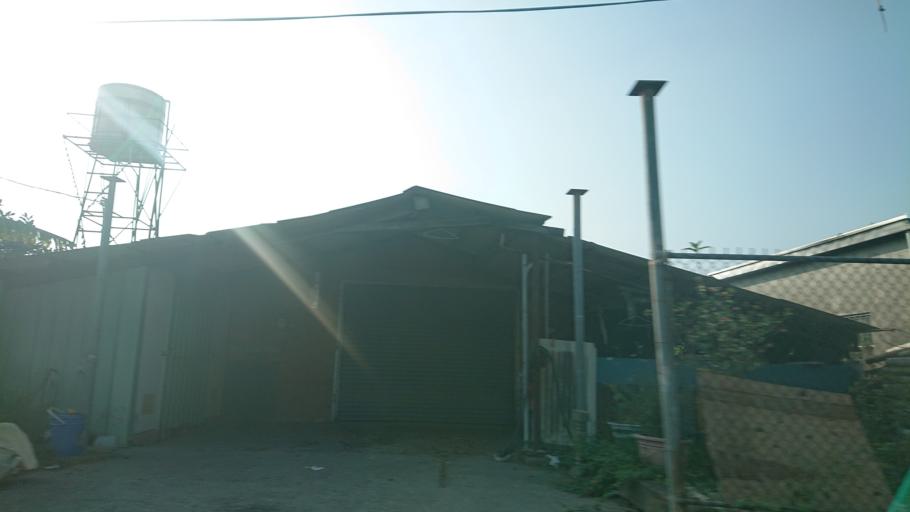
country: TW
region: Taiwan
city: Xinying
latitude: 23.1567
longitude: 120.2497
